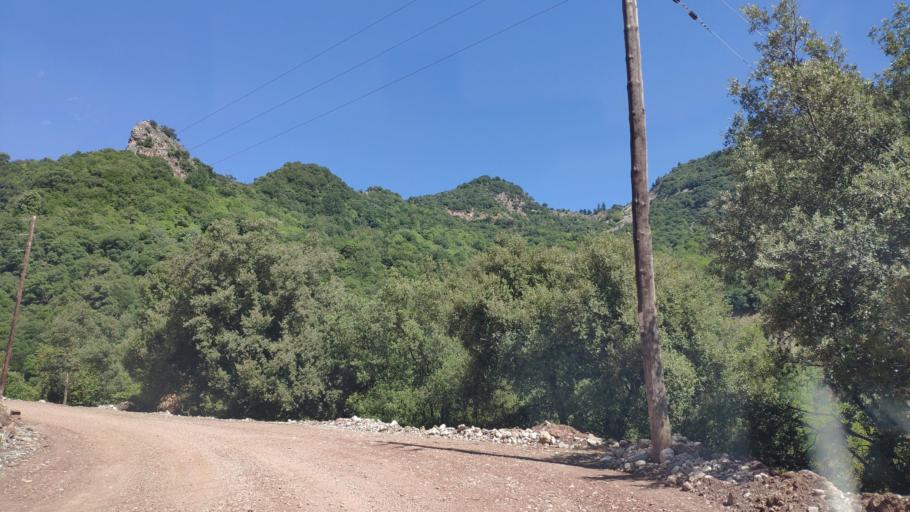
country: GR
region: Central Greece
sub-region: Nomos Evrytanias
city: Kerasochori
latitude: 39.0701
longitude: 21.6060
